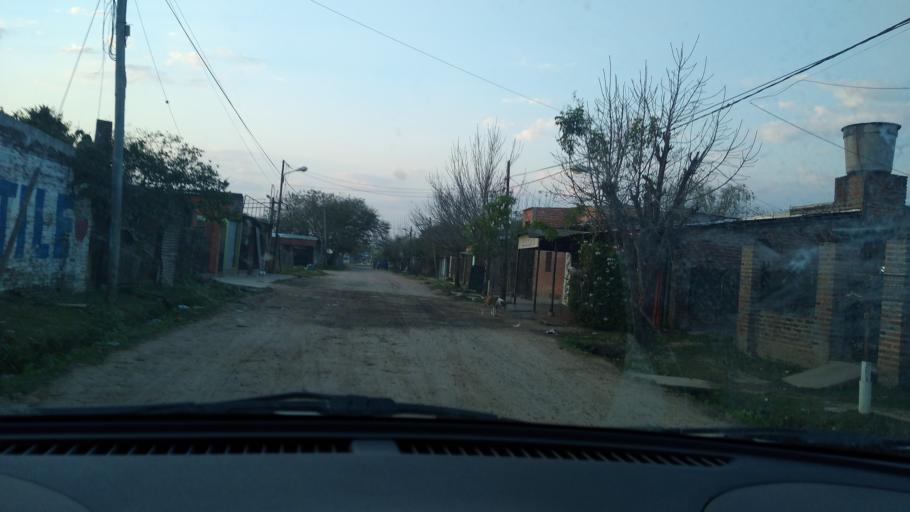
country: AR
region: Chaco
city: Resistencia
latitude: -27.4571
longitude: -58.9644
